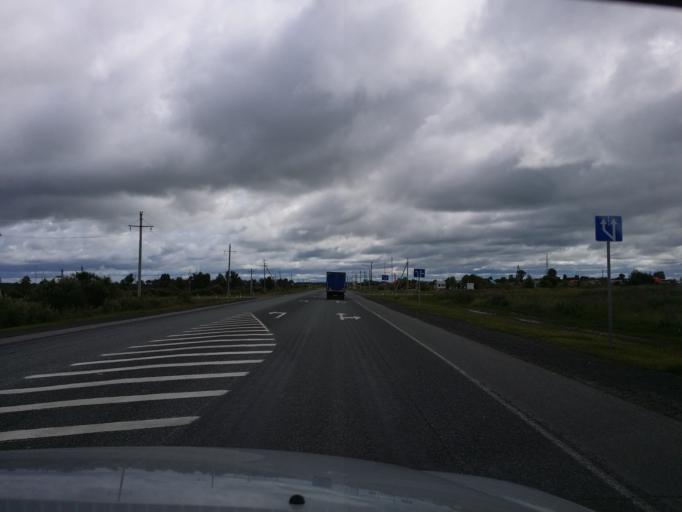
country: RU
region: Tjumen
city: Yarkovo
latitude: 57.2431
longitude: 66.7657
